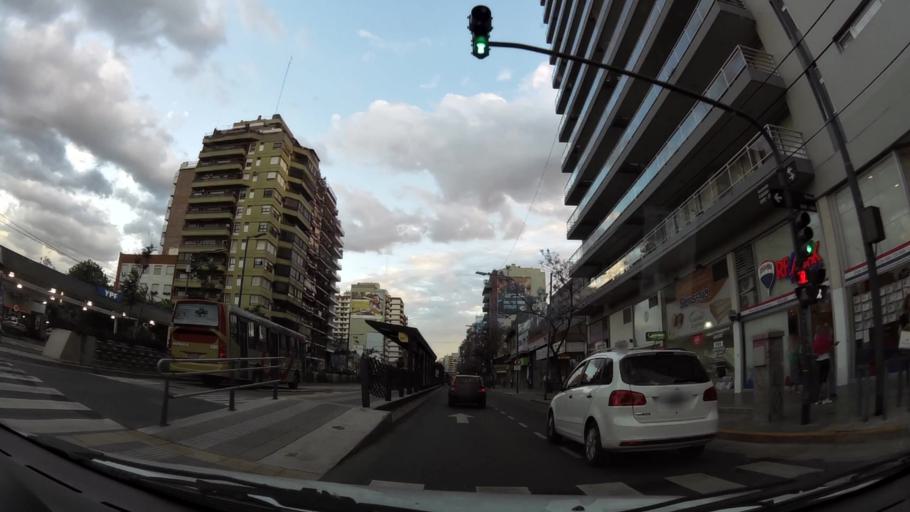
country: AR
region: Buenos Aires F.D.
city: Colegiales
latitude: -34.5502
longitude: -58.4673
